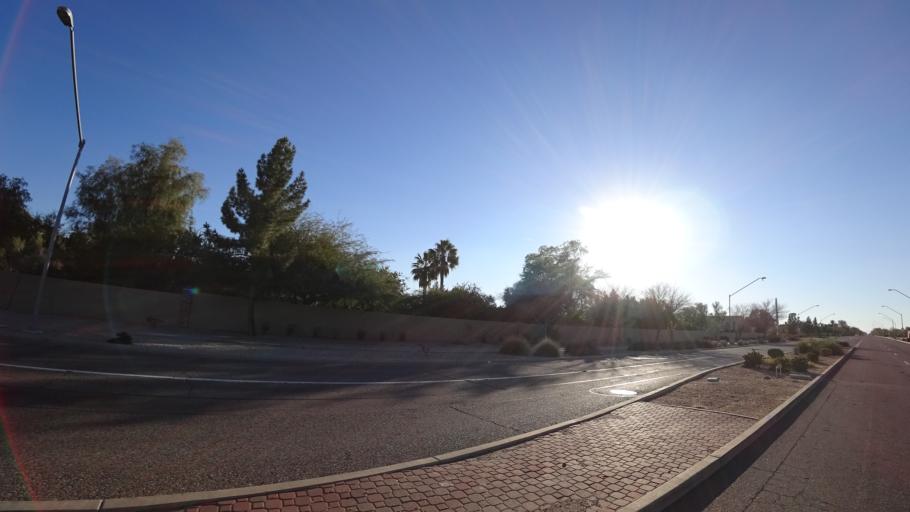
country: US
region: Arizona
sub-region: Maricopa County
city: Peoria
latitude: 33.6819
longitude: -112.2039
